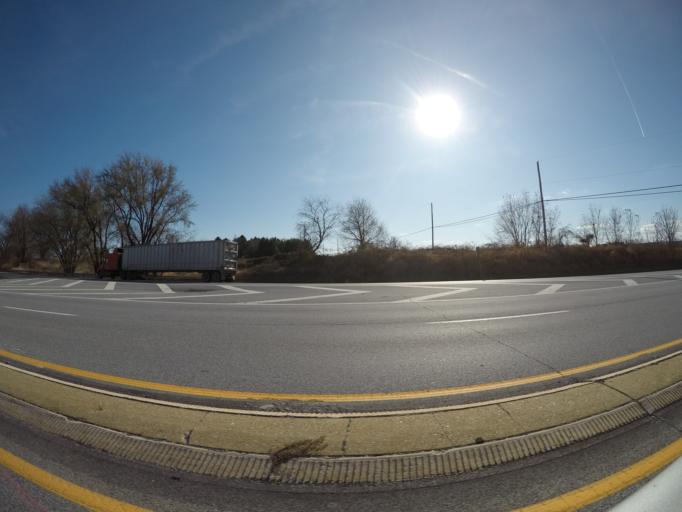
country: US
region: Pennsylvania
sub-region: Chester County
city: Parkesburg
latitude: 39.9828
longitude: -75.9256
